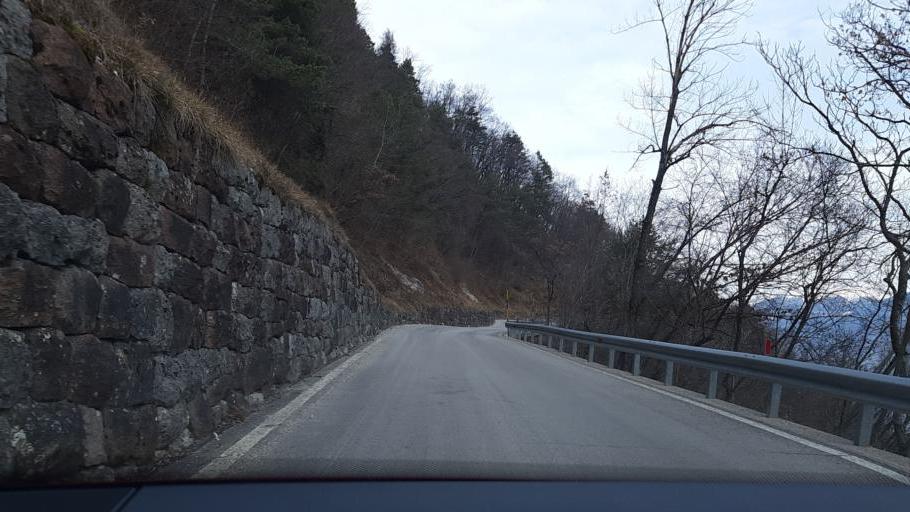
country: IT
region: Trentino-Alto Adige
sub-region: Provincia di Trento
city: Borgo
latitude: 46.0351
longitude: 11.4555
